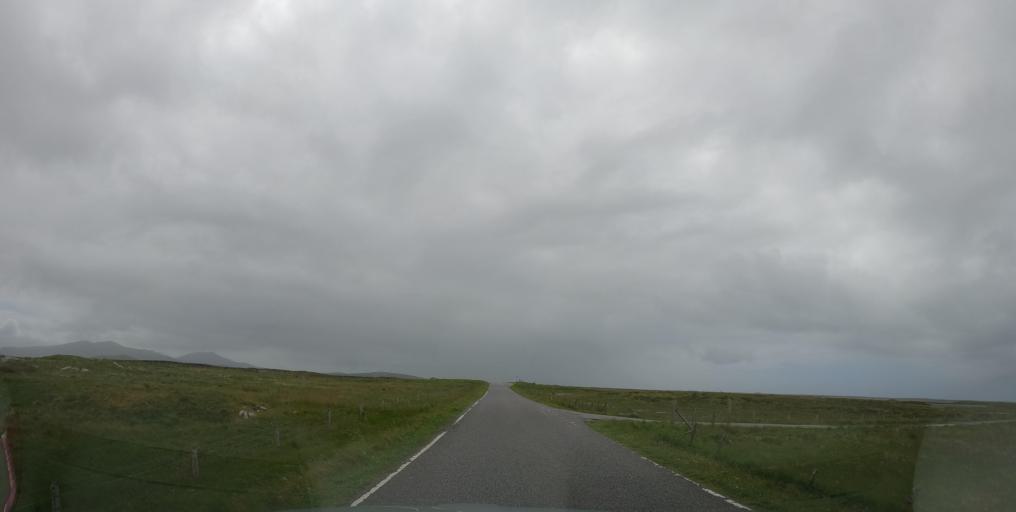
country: GB
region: Scotland
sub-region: Eilean Siar
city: Benbecula
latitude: 57.3817
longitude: -7.3414
